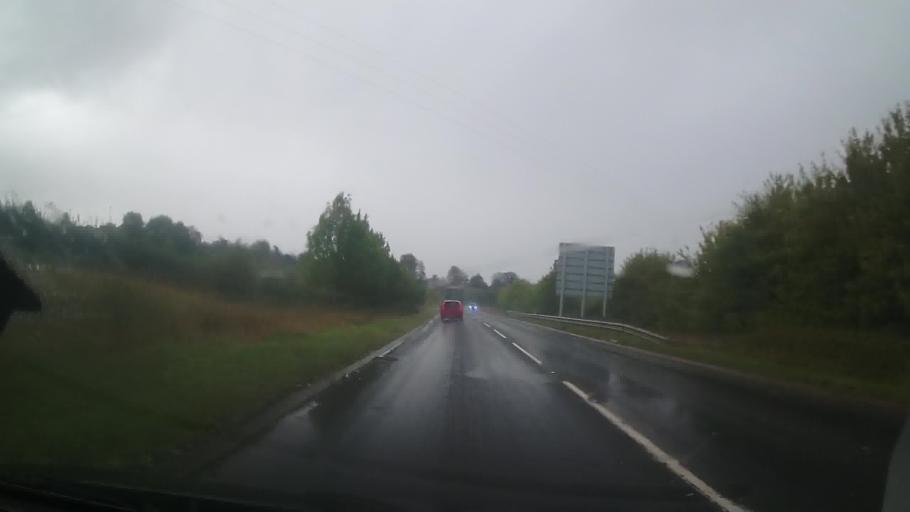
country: GB
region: England
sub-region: Worcestershire
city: Evesham
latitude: 52.1126
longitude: -1.9486
